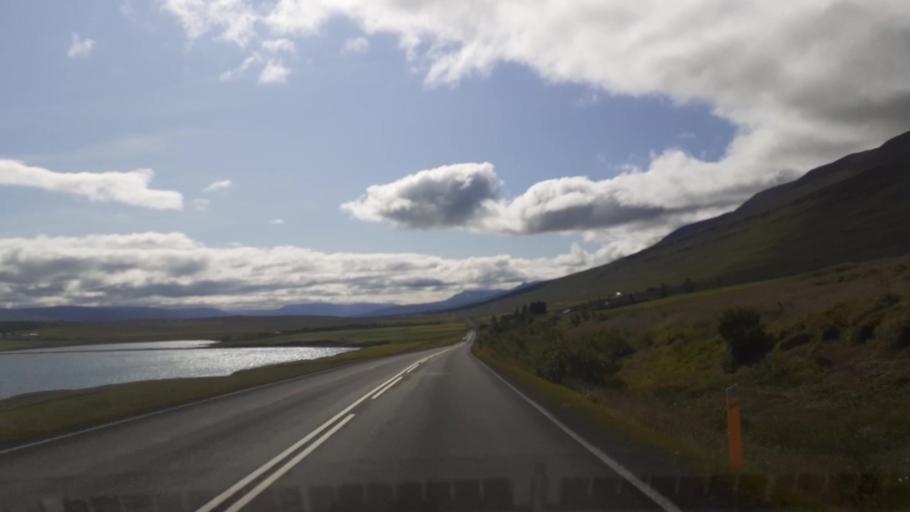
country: IS
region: Northeast
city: Akureyri
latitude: 65.8759
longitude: -18.2649
